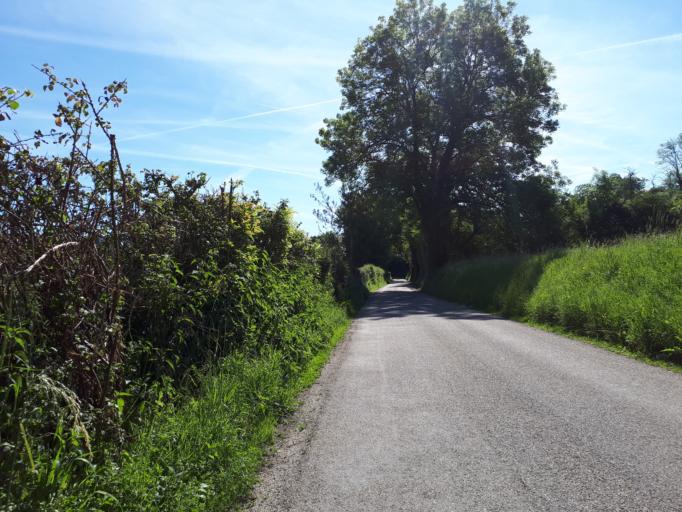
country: FR
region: Rhone-Alpes
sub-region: Departement de l'Isere
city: Saint-Savin
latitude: 45.6118
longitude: 5.3067
